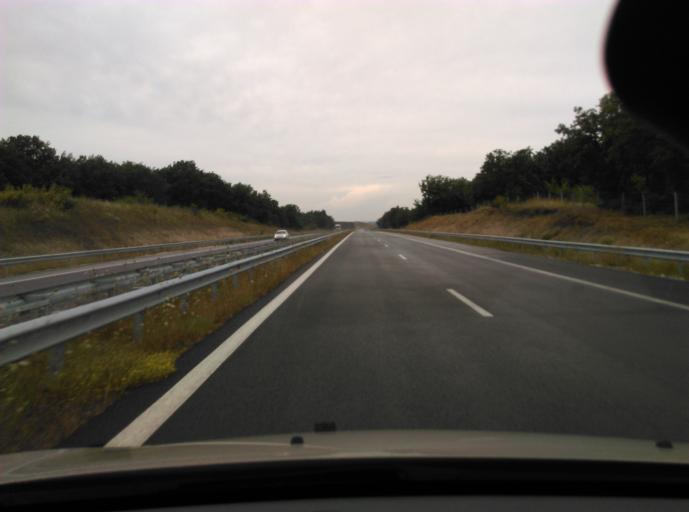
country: BG
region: Khaskovo
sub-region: Obshtina Dimitrovgrad
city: Dimitrovgrad
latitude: 42.0518
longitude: 25.4936
